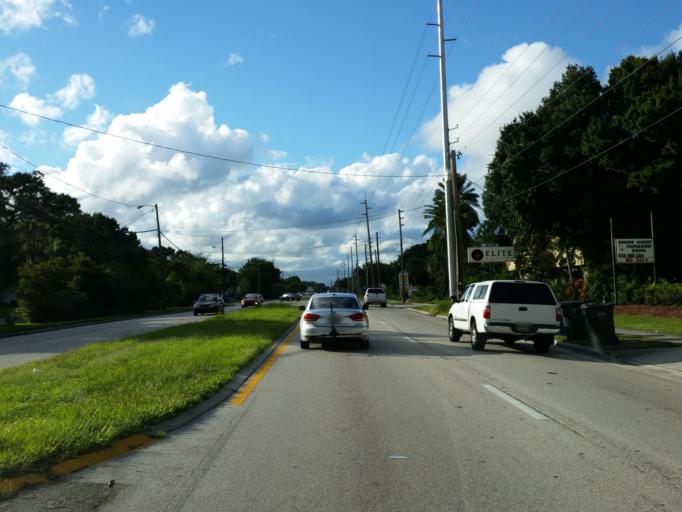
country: US
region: Florida
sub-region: Hillsborough County
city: Town 'n' Country
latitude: 27.9921
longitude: -82.5770
